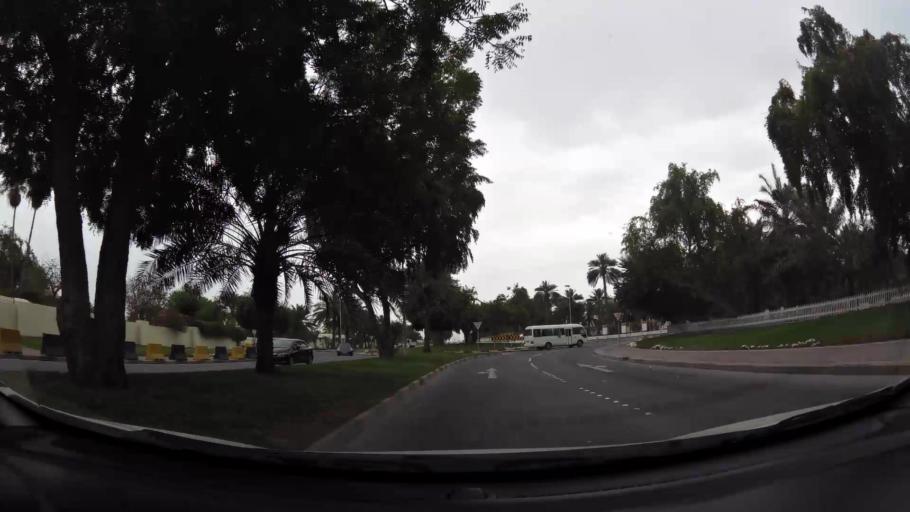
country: BH
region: Northern
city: Ar Rifa'
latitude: 26.1219
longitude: 50.5359
